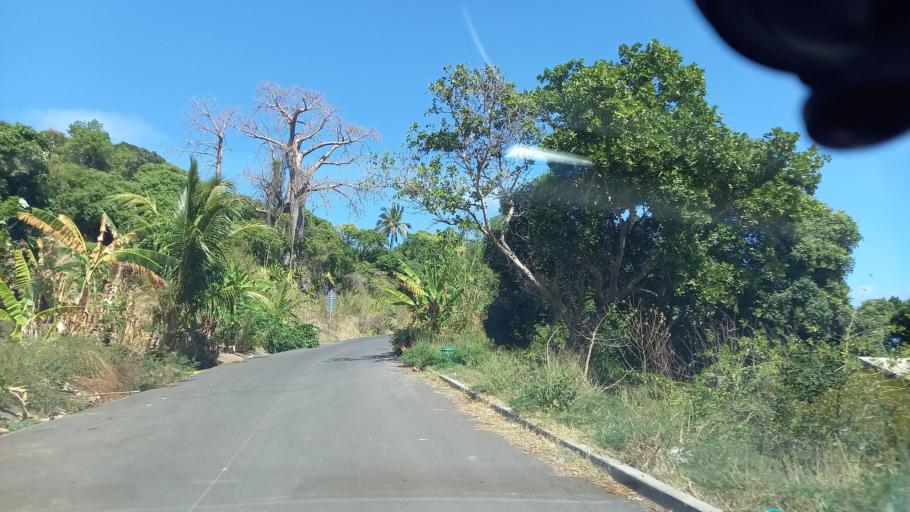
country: YT
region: Kani-Keli
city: Kani Keli
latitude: -12.9668
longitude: 45.1116
